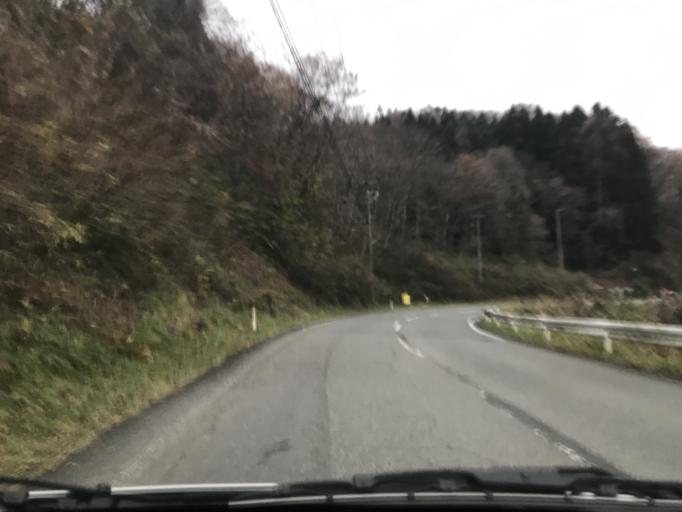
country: JP
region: Iwate
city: Mizusawa
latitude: 39.0366
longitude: 141.3428
